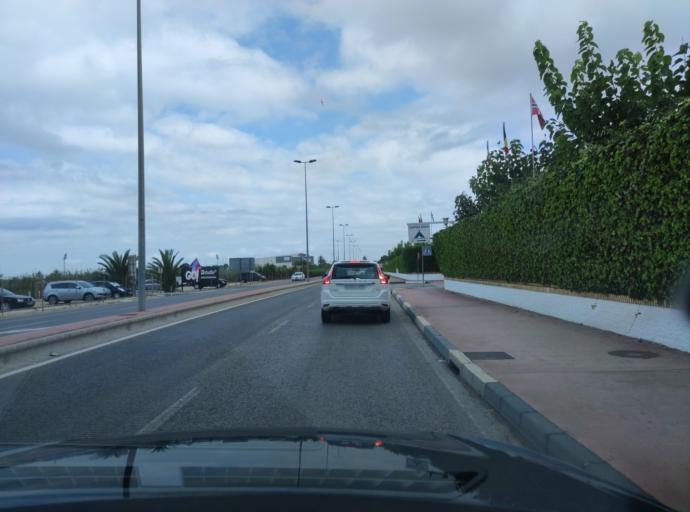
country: ES
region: Valencia
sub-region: Provincia de Alicante
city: Santa Pola
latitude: 38.2003
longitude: -0.5696
